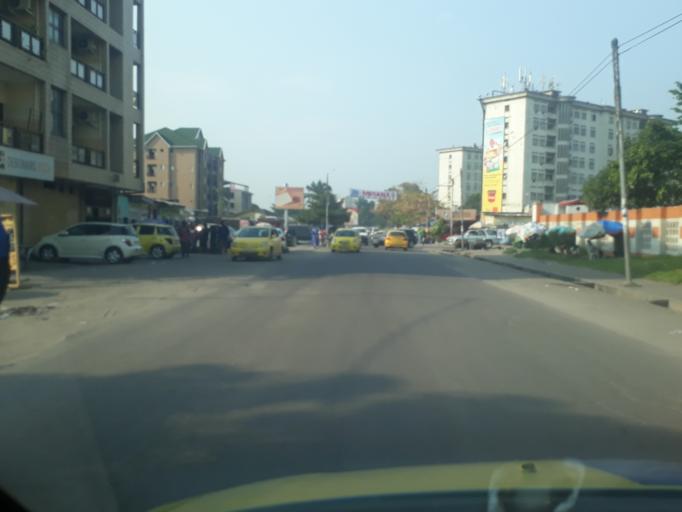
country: CD
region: Kinshasa
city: Kinshasa
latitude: -4.3186
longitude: 15.3300
